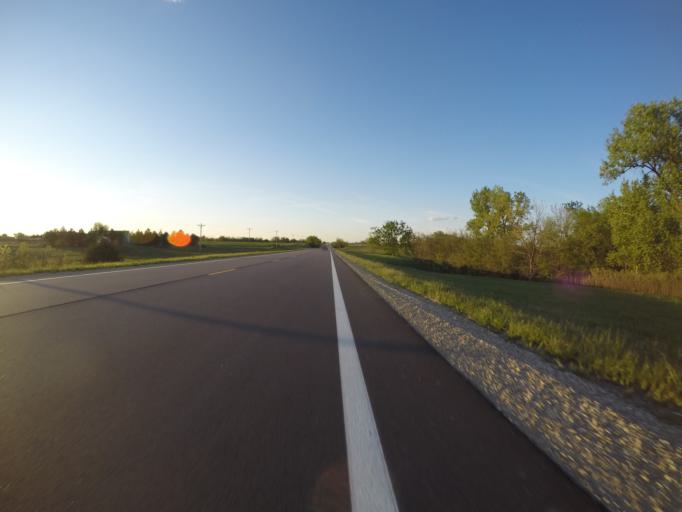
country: US
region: Kansas
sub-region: Pottawatomie County
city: Westmoreland
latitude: 39.3811
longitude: -96.5198
